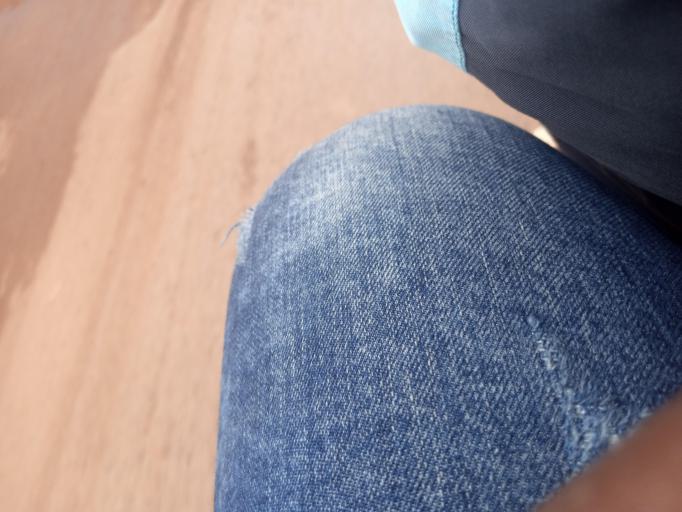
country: SL
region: Southern Province
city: Bo
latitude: 7.9682
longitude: -11.7373
